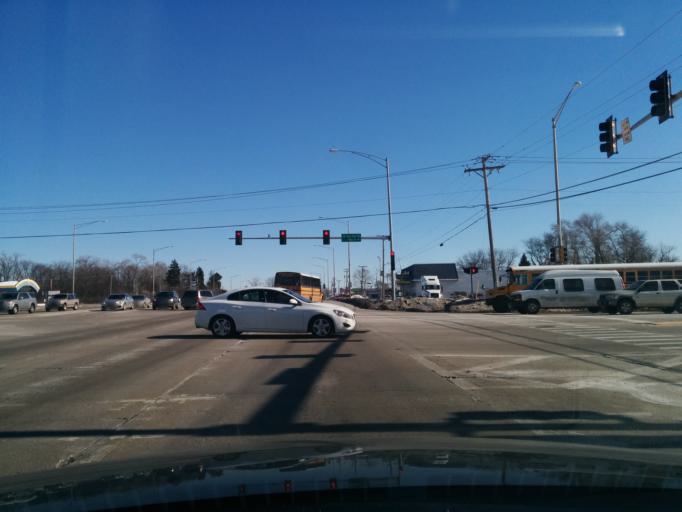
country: US
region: Illinois
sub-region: DuPage County
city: Glendale Heights
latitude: 41.9033
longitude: -88.0635
